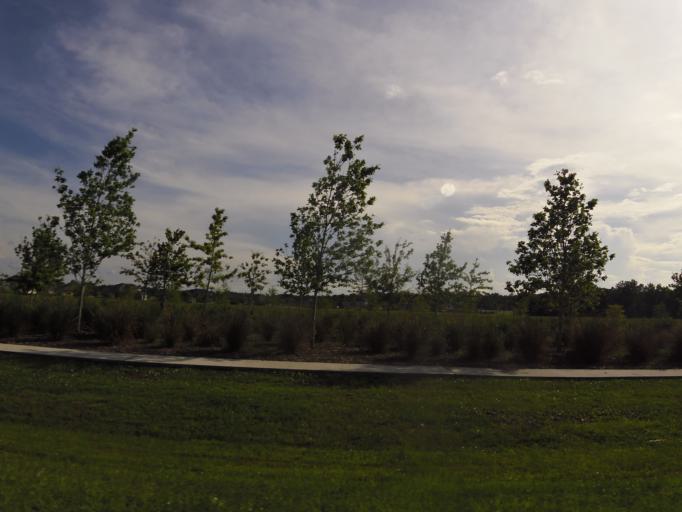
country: US
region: Florida
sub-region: Clay County
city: Green Cove Springs
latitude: 29.9841
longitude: -81.5242
